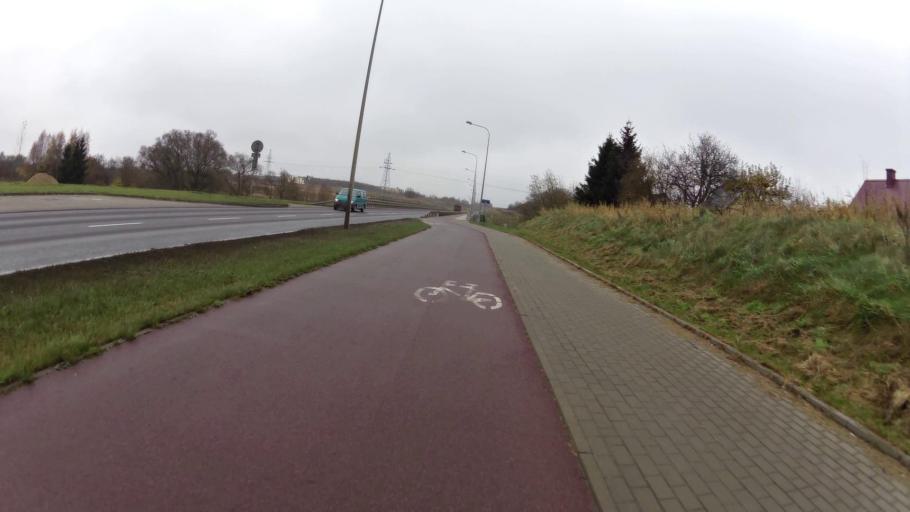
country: PL
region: West Pomeranian Voivodeship
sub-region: Koszalin
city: Koszalin
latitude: 54.2106
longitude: 16.1674
